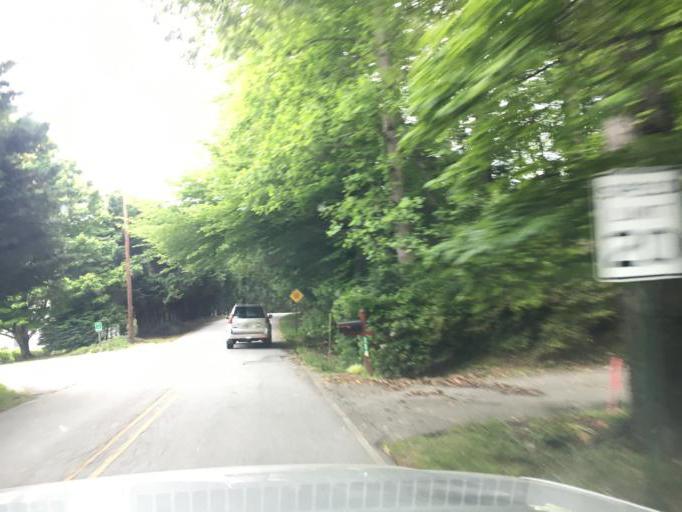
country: US
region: North Carolina
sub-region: Transylvania County
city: Brevard
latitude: 35.2485
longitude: -82.7240
